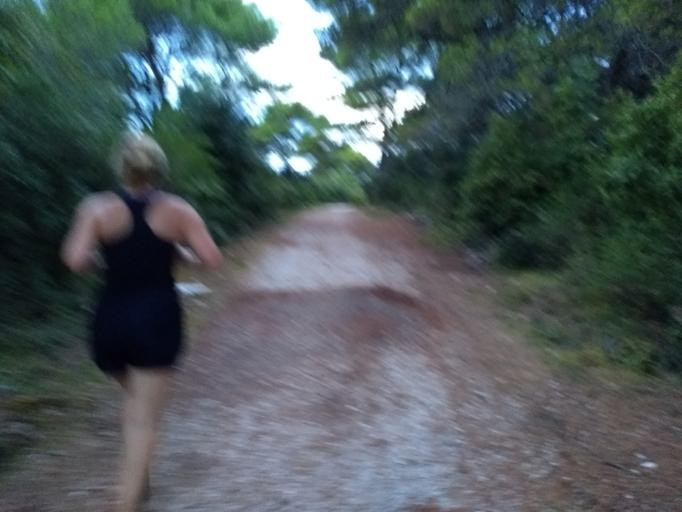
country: HR
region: Zadarska
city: Ugljan
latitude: 44.1339
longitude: 15.0688
